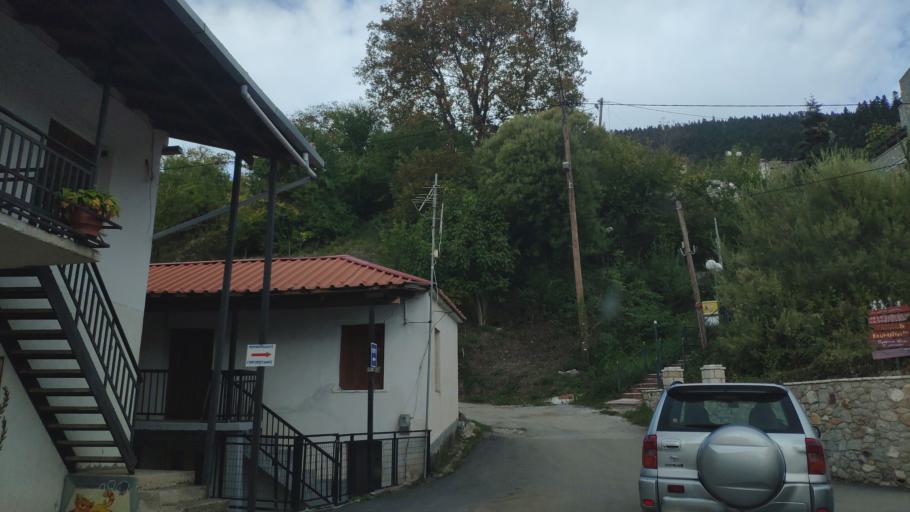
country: GR
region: Central Greece
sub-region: Nomos Fthiotidos
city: Stavros
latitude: 38.7407
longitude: 22.3368
